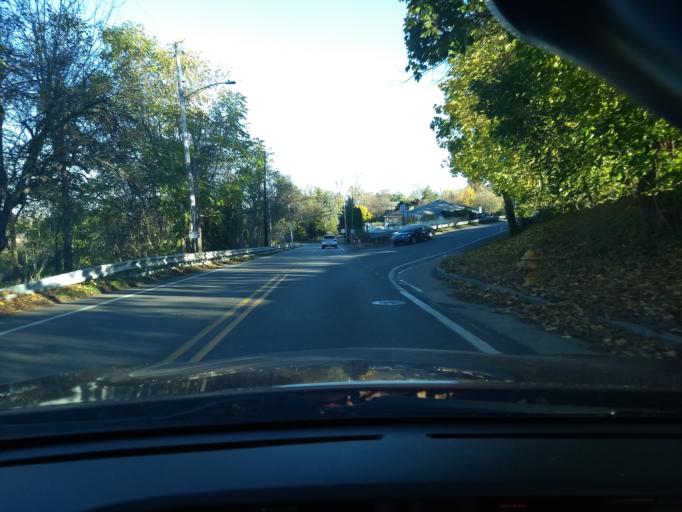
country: US
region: Pennsylvania
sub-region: Allegheny County
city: Rennerdale
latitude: 40.3786
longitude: -80.1616
